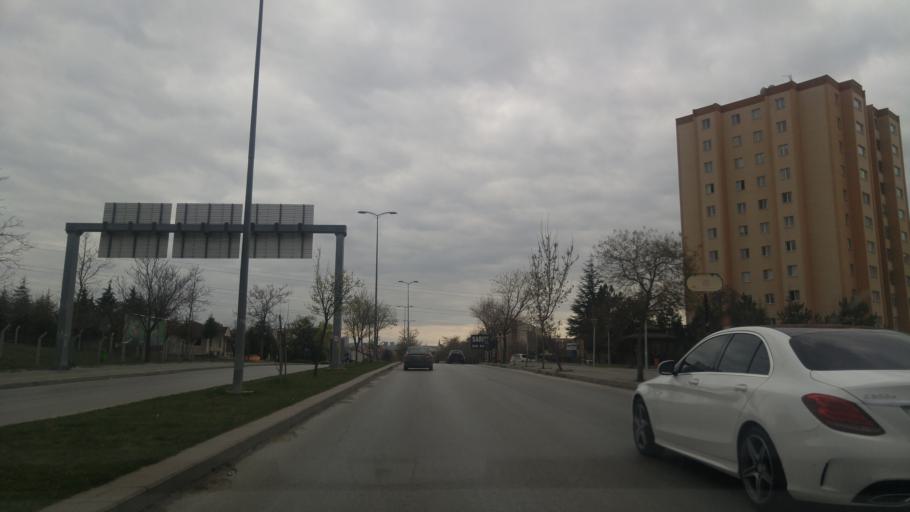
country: TR
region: Ankara
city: Etimesgut
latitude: 39.8831
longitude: 32.6901
